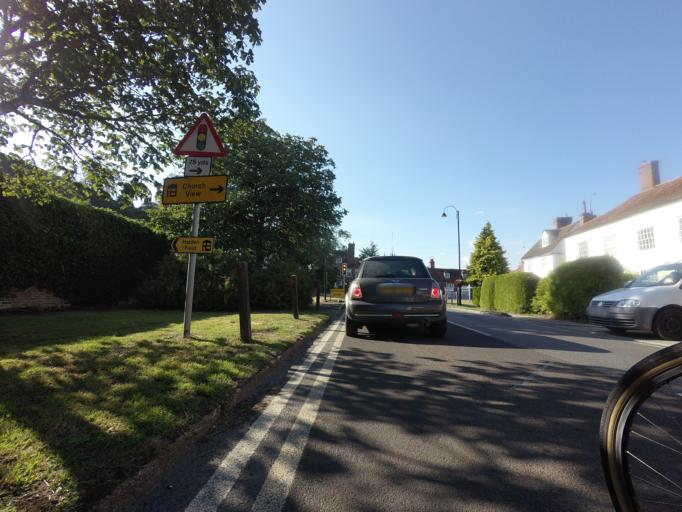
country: GB
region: England
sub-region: Kent
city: Tenterden
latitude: 51.0659
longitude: 0.6811
